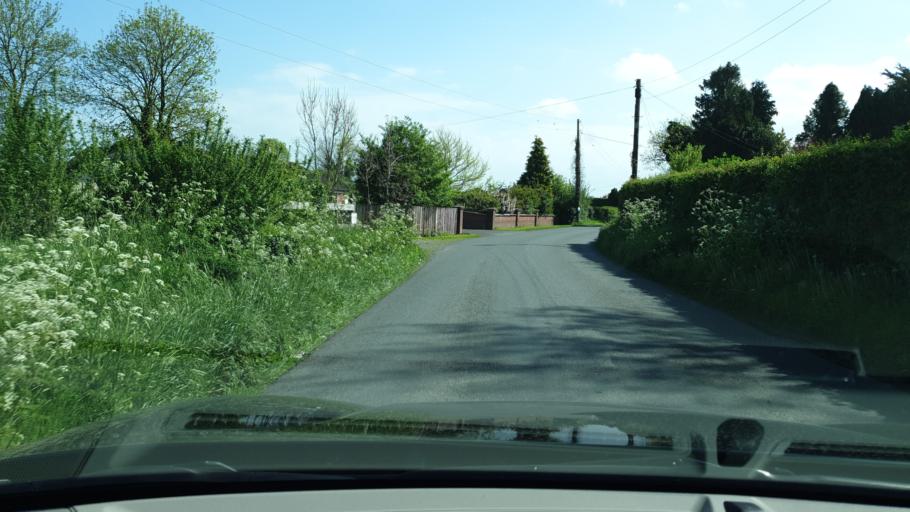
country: IE
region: Leinster
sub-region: Kildare
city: Maynooth
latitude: 53.4108
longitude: -6.5761
